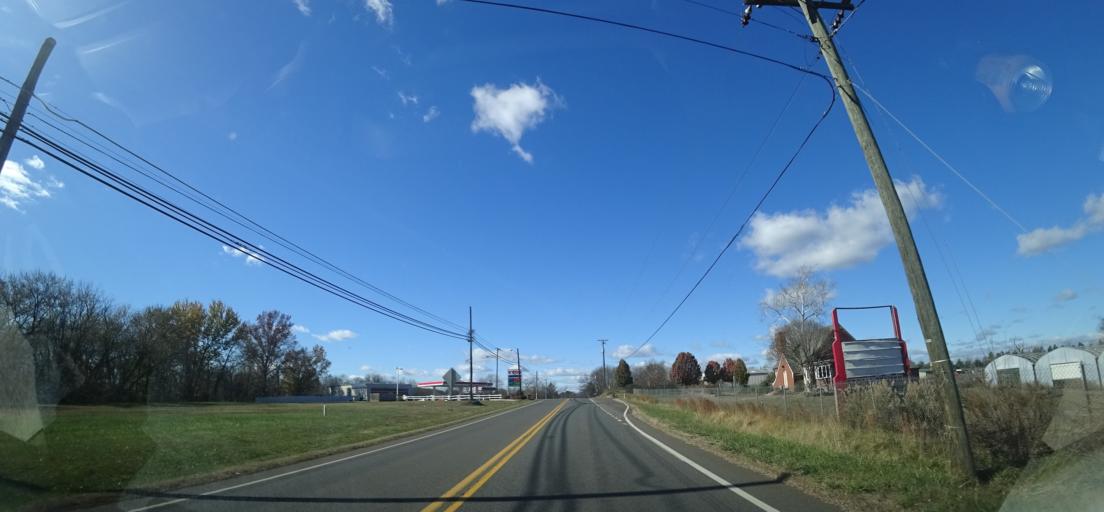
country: US
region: Virginia
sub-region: Culpeper County
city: Culpeper
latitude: 38.4875
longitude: -77.9450
